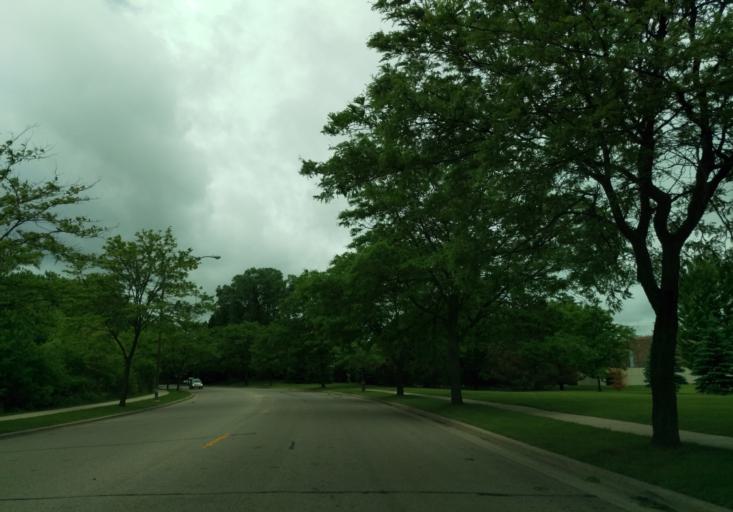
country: US
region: Wisconsin
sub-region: Dane County
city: Middleton
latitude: 43.0481
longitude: -89.4911
